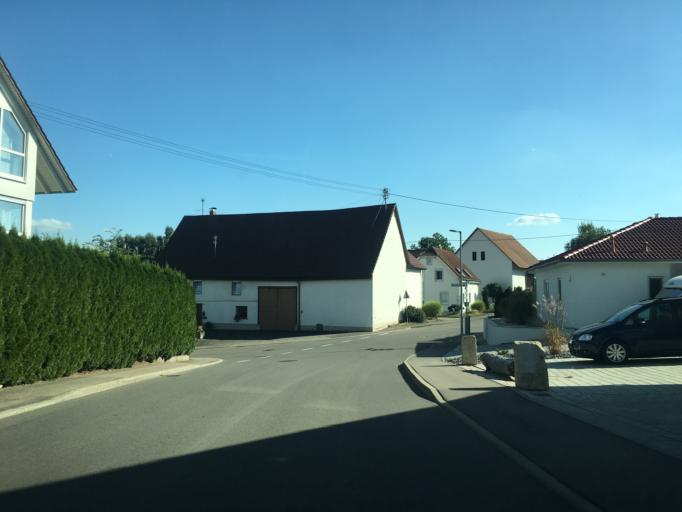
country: DE
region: Baden-Wuerttemberg
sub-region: Tuebingen Region
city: Obermarchtal
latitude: 48.2332
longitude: 9.5686
